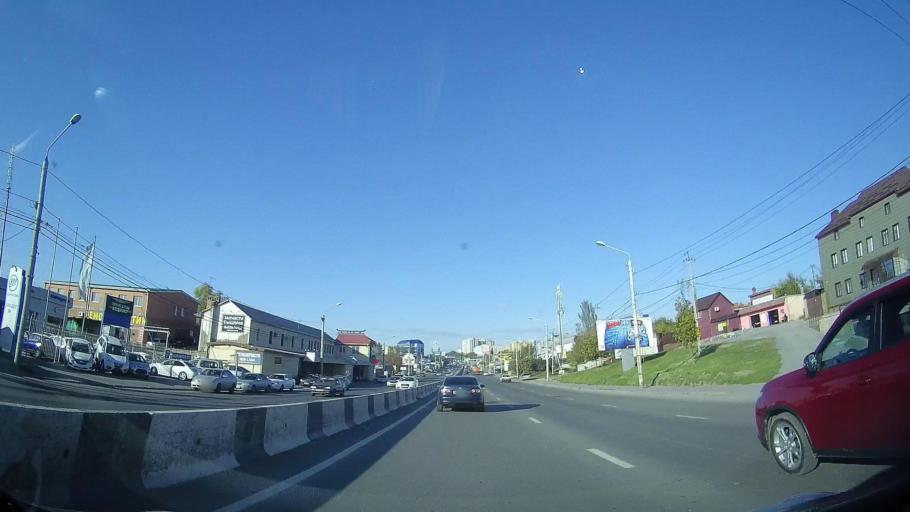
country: RU
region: Rostov
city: Kalinin
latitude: 47.2196
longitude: 39.6134
